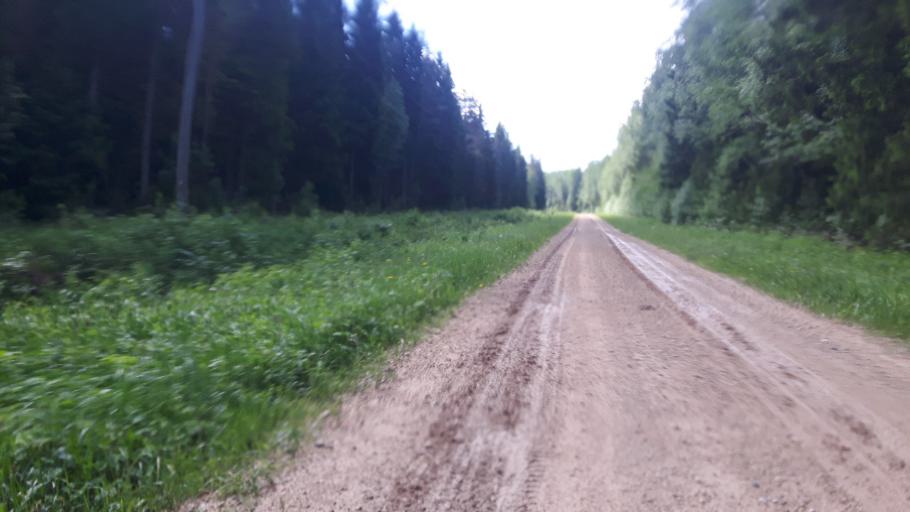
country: EE
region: Paernumaa
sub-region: Vaendra vald (alev)
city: Vandra
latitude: 58.7151
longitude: 25.0423
